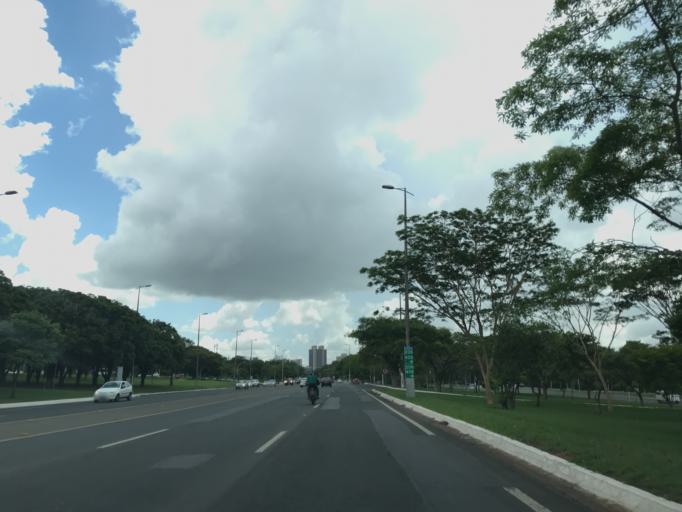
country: BR
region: Federal District
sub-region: Brasilia
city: Brasilia
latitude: -15.8148
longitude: -47.8978
